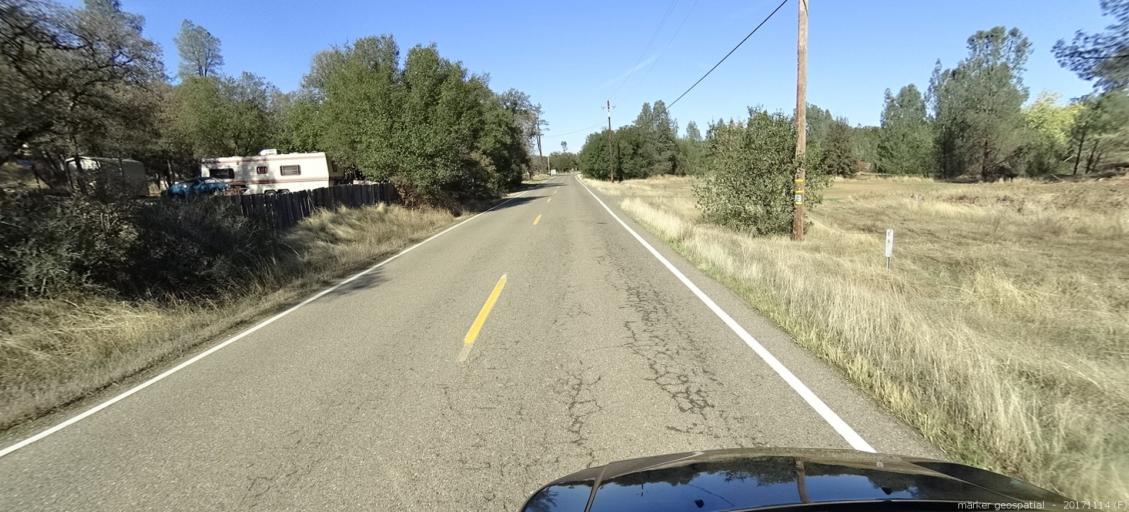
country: US
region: California
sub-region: Shasta County
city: Cottonwood
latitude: 40.3973
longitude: -122.3511
